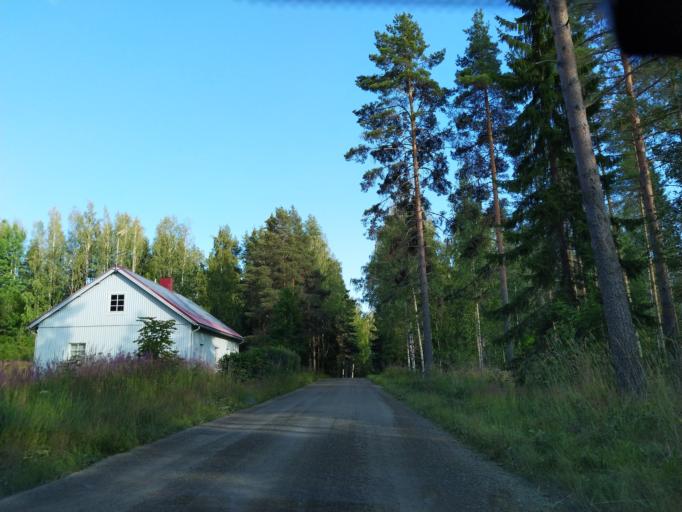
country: FI
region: Central Finland
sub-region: Jaemsae
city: Kuhmoinen
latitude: 61.6862
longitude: 24.9678
